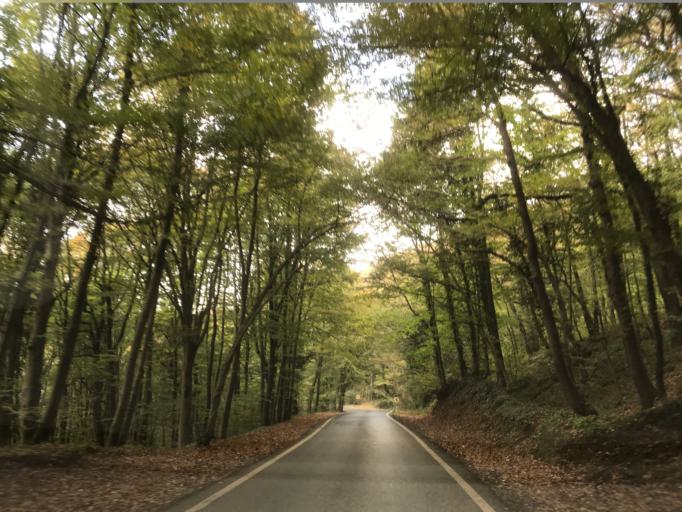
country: TR
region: Istanbul
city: Arikoey
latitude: 41.1883
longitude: 28.9828
